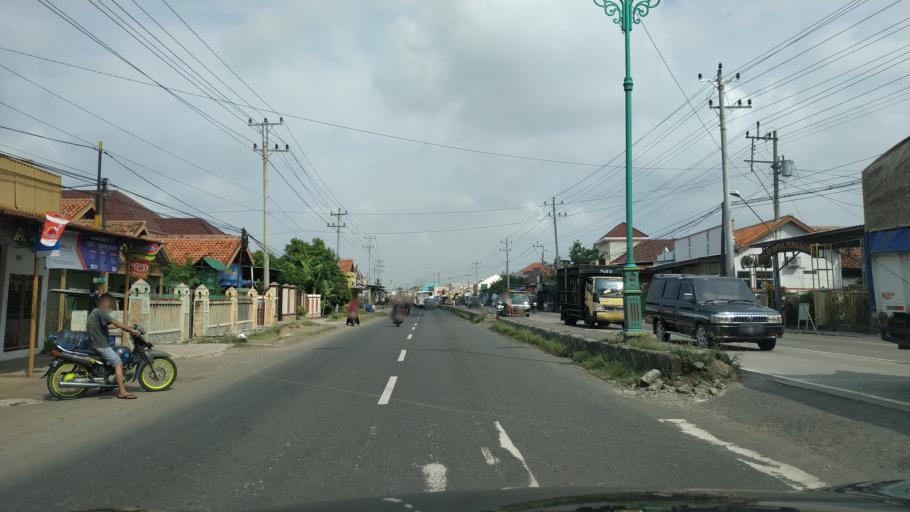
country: ID
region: Central Java
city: Bulakamba
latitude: -6.8745
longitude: 108.9233
